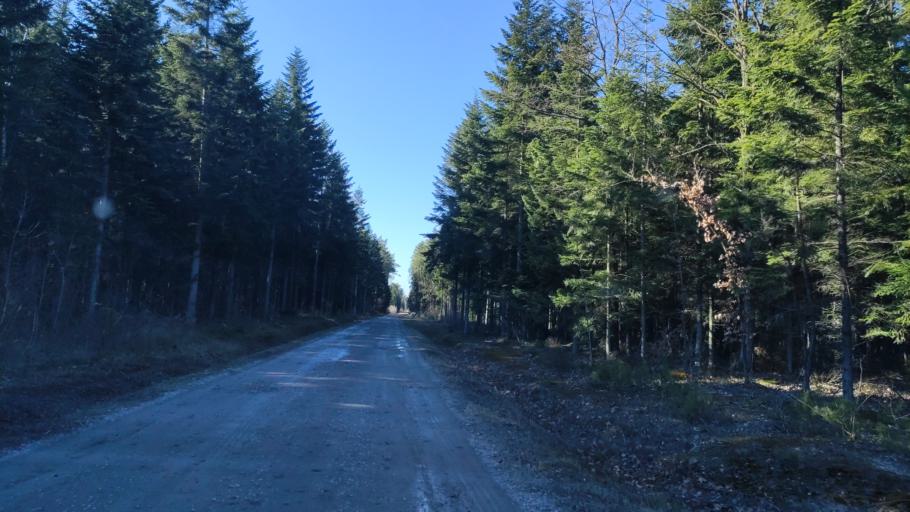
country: PL
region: Masovian Voivodeship
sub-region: Powiat radomski
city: Jedlnia-Letnisko
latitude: 51.4658
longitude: 21.3158
